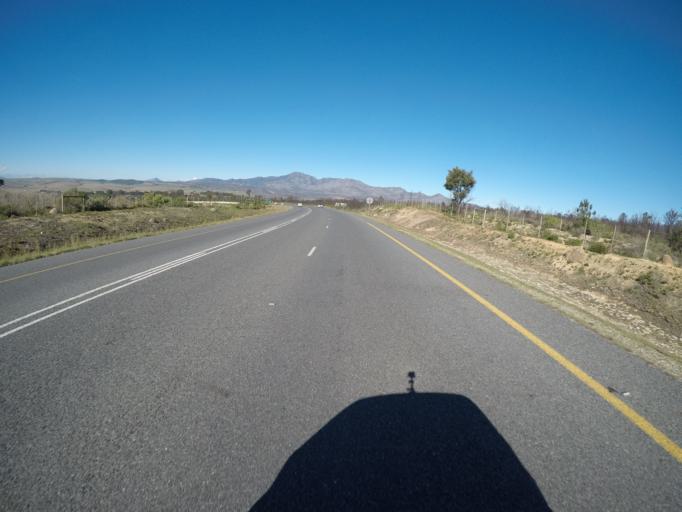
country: ZA
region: Western Cape
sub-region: Overberg District Municipality
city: Grabouw
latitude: -34.2324
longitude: 19.1887
